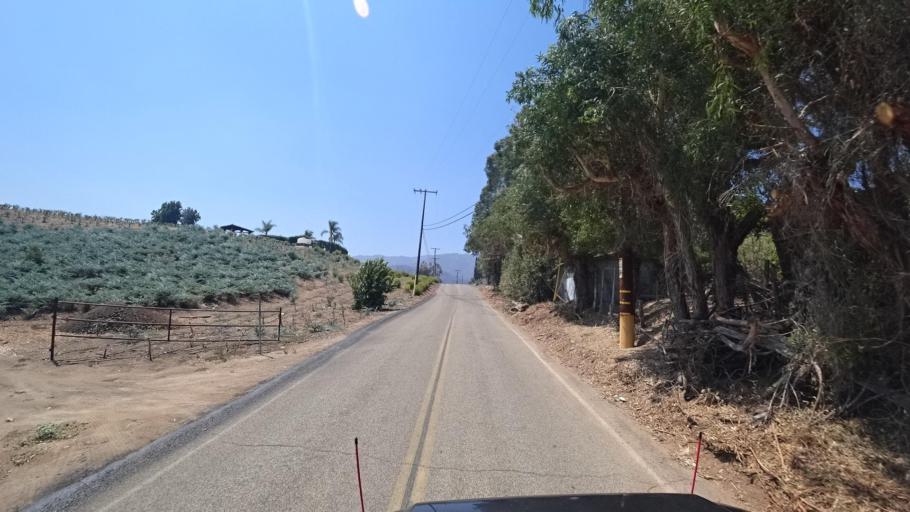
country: US
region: California
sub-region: San Diego County
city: Fallbrook
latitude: 33.4340
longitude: -117.3071
